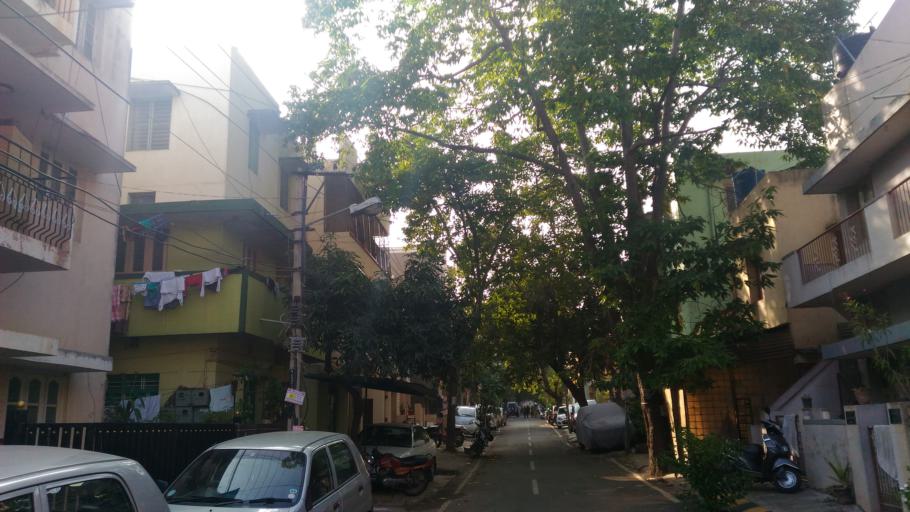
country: IN
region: Karnataka
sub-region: Bangalore Urban
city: Bangalore
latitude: 12.9222
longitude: 77.5966
